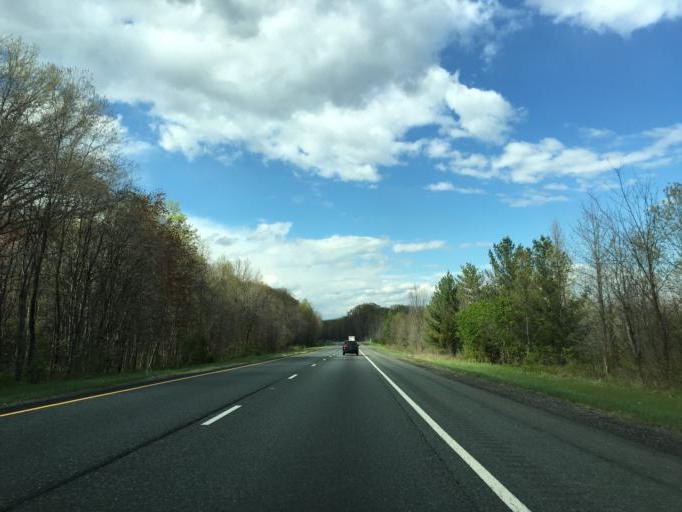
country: US
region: Maryland
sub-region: Baltimore County
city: Edgemere
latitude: 39.2578
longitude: -76.4578
